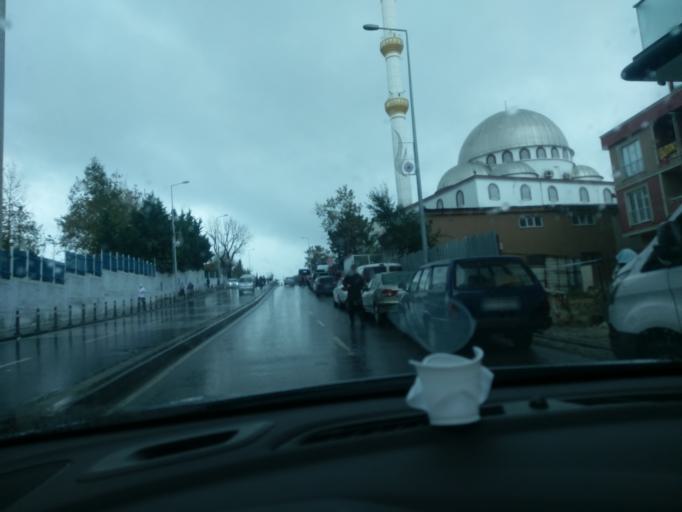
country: TR
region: Istanbul
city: Sisli
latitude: 41.0889
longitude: 28.9676
